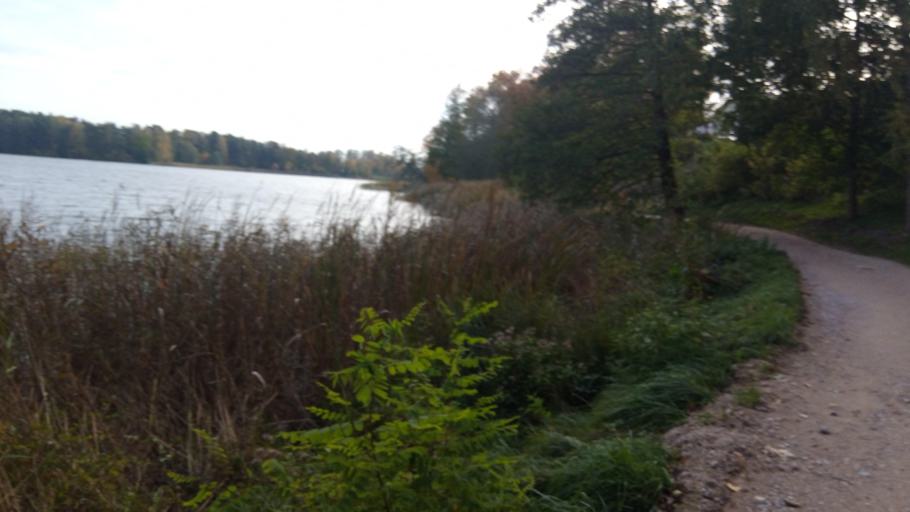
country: LT
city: Trakai
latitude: 54.6352
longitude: 24.9396
